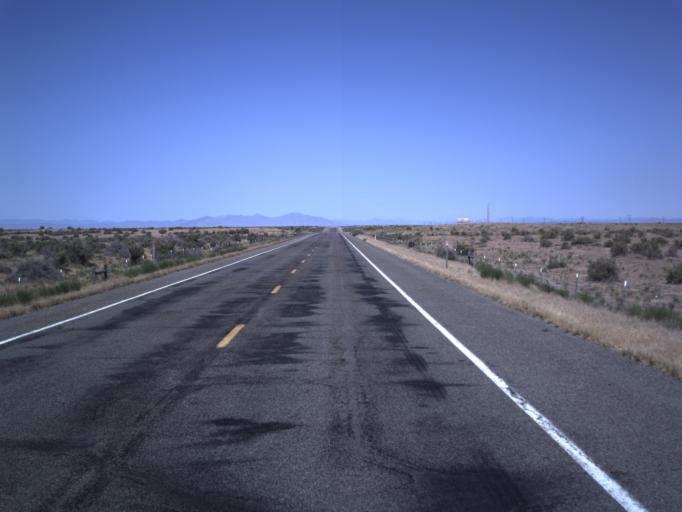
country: US
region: Utah
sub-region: Millard County
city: Delta
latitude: 39.4726
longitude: -112.4716
